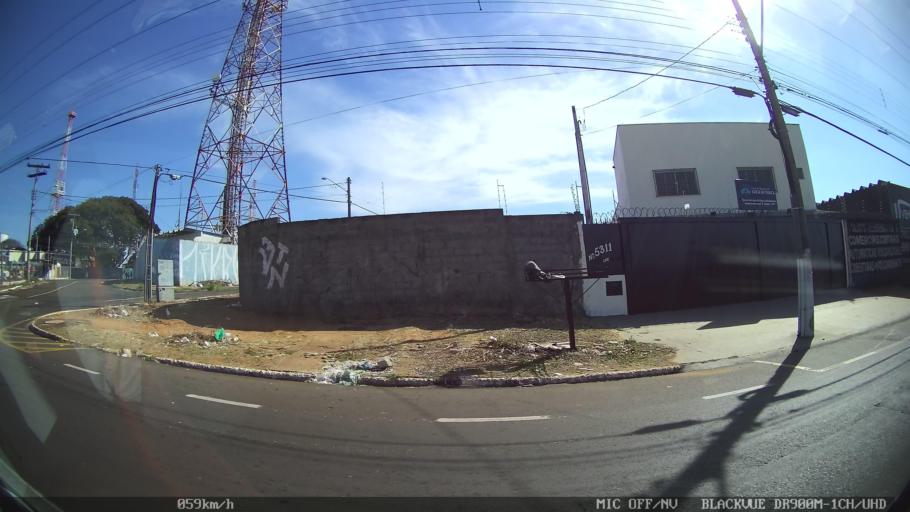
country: BR
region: Sao Paulo
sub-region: Franca
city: Franca
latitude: -20.5042
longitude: -47.3992
